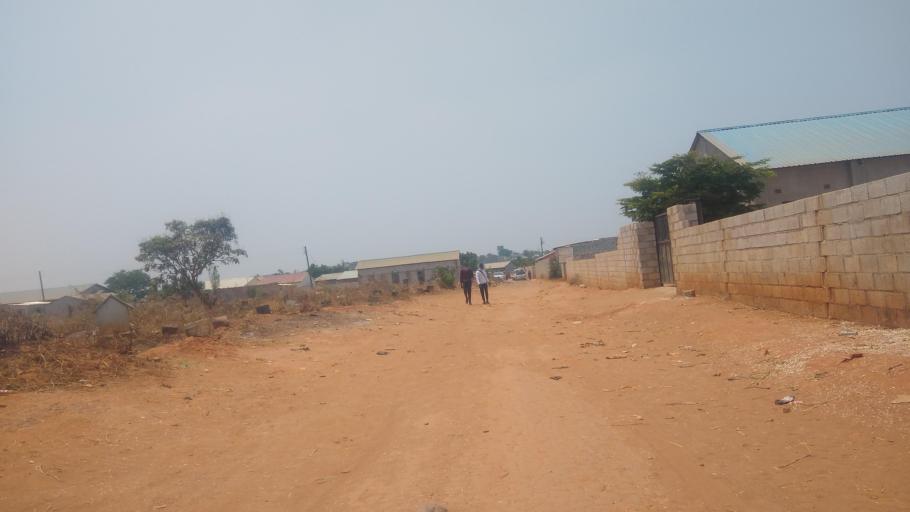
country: ZM
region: Lusaka
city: Lusaka
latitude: -15.4375
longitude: 28.3758
